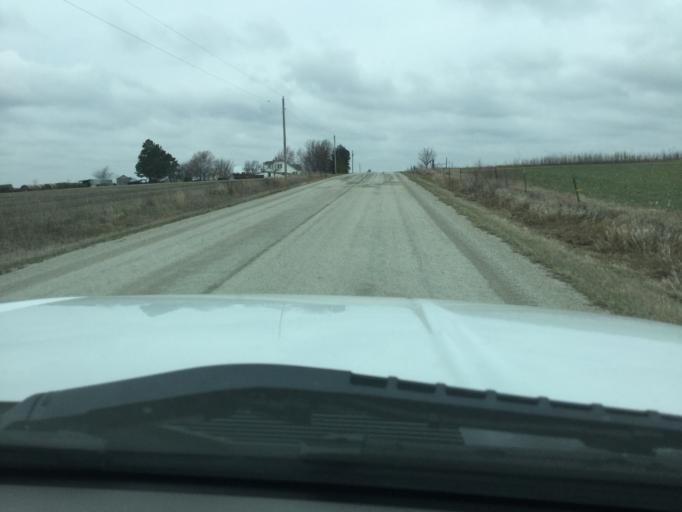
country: US
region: Kansas
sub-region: Nemaha County
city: Sabetha
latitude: 39.7980
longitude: -95.7603
